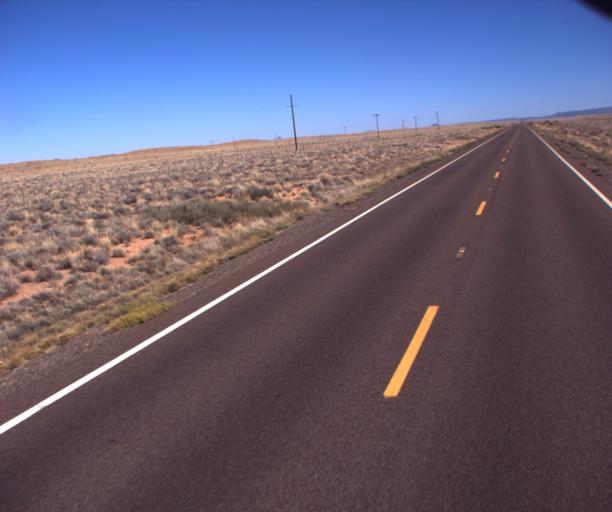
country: US
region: Arizona
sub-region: Navajo County
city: Winslow
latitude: 35.1226
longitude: -110.5065
